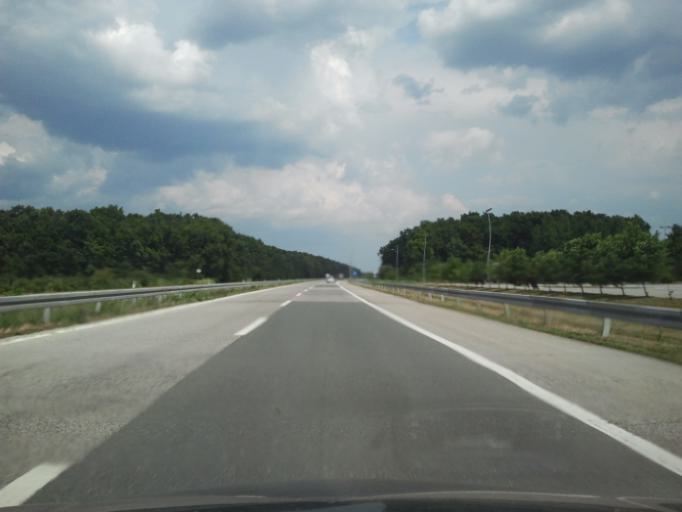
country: RS
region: Autonomna Pokrajina Vojvodina
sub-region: Sremski Okrug
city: Sid
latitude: 45.0474
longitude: 19.2254
